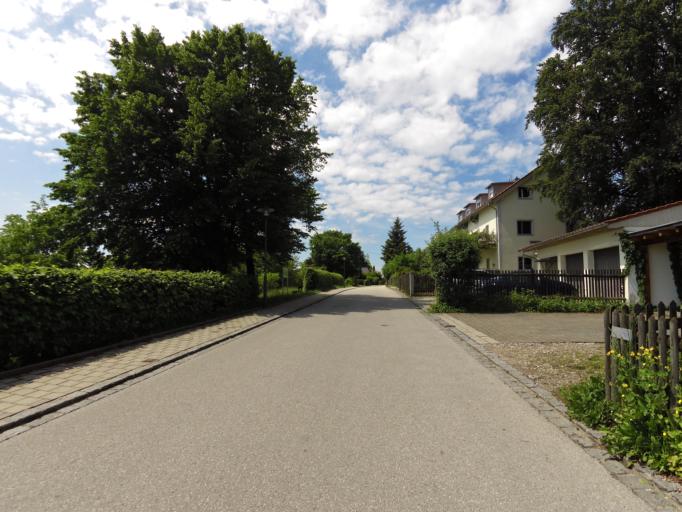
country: DE
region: Bavaria
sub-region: Upper Bavaria
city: Schaftlarn
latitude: 47.9900
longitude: 11.4499
